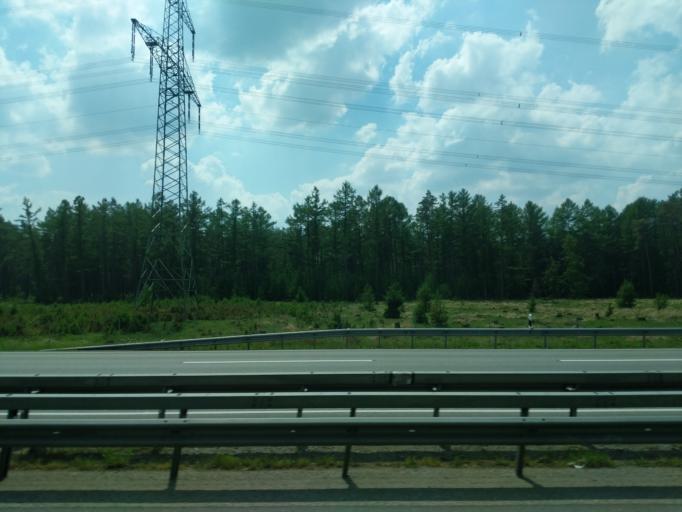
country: DE
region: Schleswig-Holstein
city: Gudow
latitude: 53.5228
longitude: 10.7970
